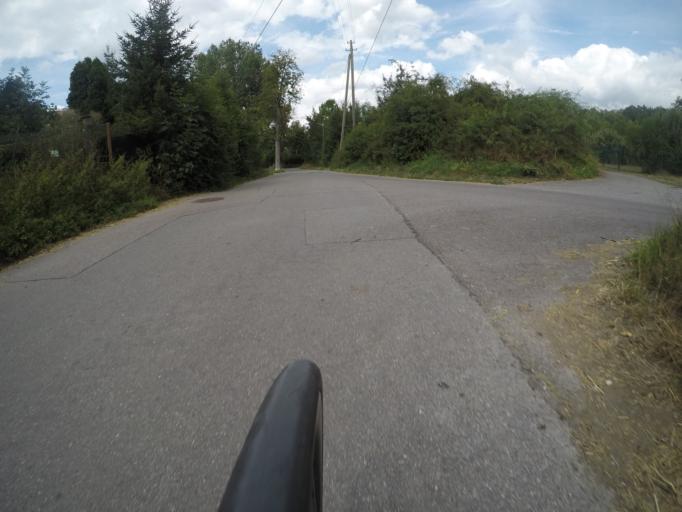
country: DE
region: Baden-Wuerttemberg
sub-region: Regierungsbezirk Stuttgart
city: Weil der Stadt
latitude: 48.7452
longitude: 8.8772
